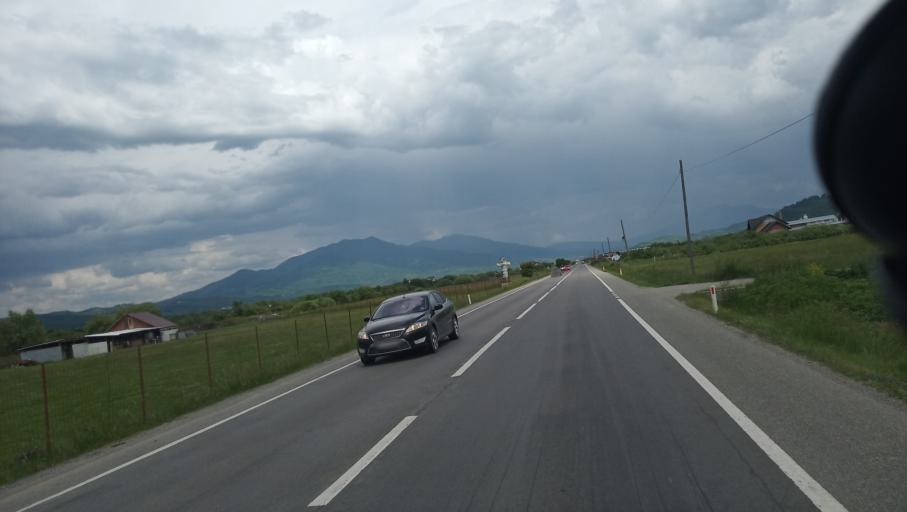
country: RO
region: Bistrita-Nasaud
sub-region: Comuna Livezile
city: Livezile
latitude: 47.1894
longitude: 24.6072
